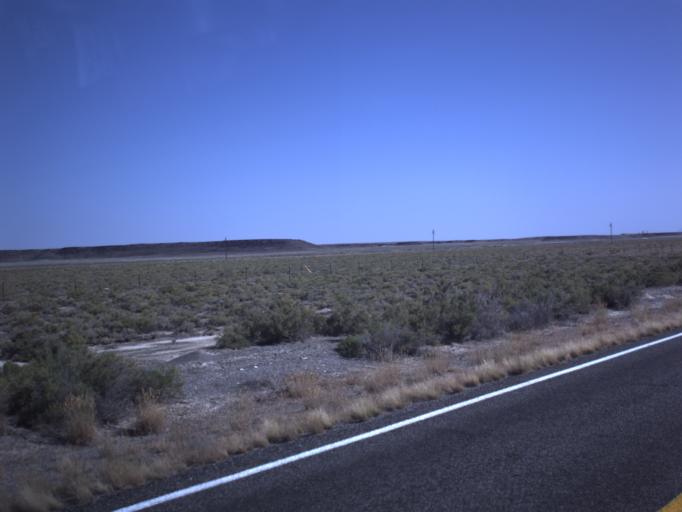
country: US
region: Utah
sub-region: Millard County
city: Delta
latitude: 39.1533
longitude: -112.7172
